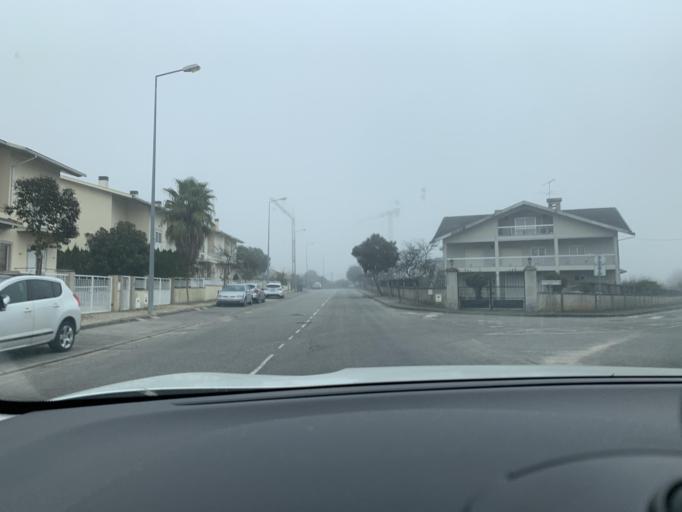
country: PT
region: Viseu
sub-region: Viseu
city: Viseu
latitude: 40.6397
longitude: -7.9188
